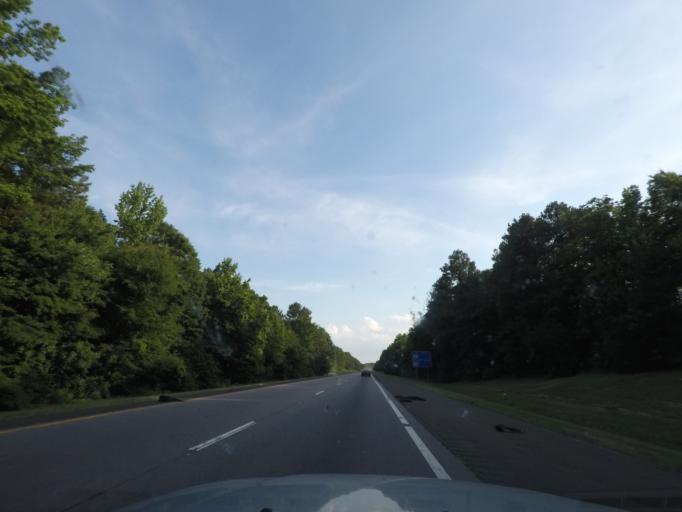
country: US
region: North Carolina
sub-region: Granville County
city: Butner
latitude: 36.0915
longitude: -78.7615
